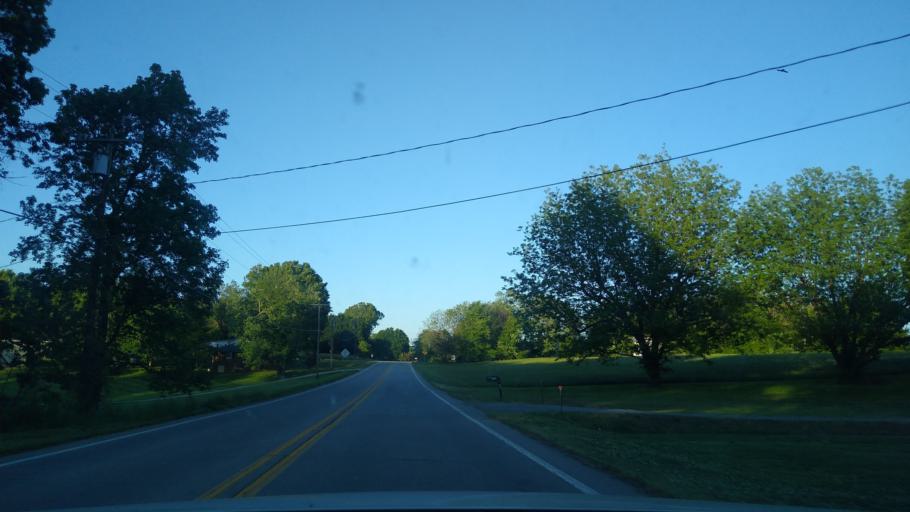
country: US
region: North Carolina
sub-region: Rockingham County
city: Reidsville
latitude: 36.3681
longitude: -79.6130
